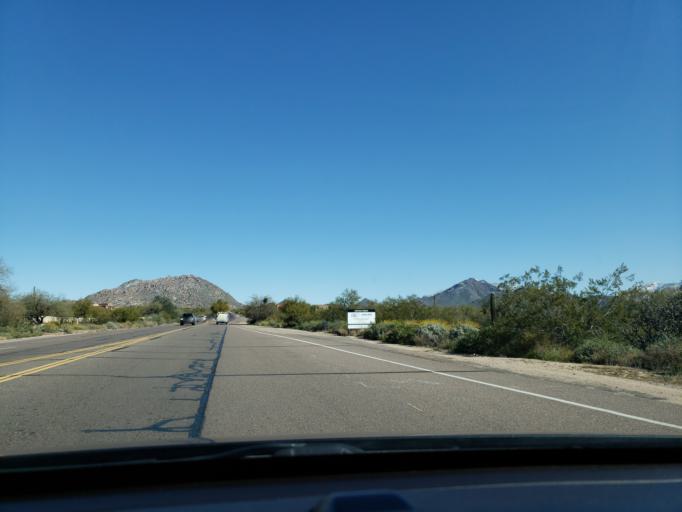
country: US
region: Arizona
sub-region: Maricopa County
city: Carefree
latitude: 33.7126
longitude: -111.8871
